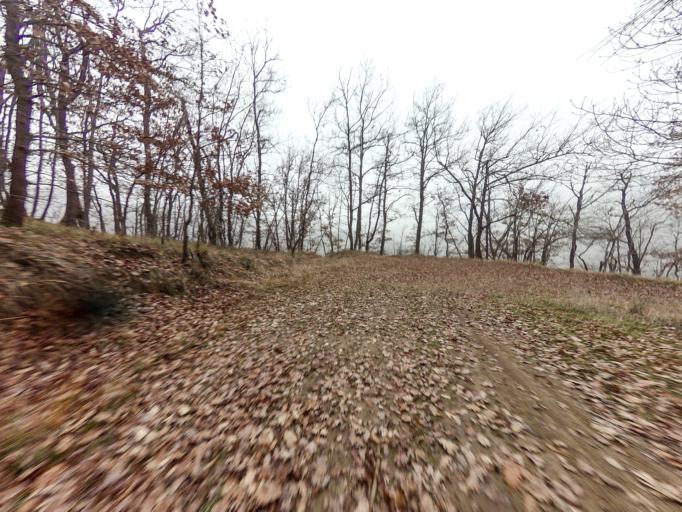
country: IT
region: Emilia-Romagna
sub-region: Provincia di Bologna
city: Pianoro
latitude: 44.3388
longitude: 11.3205
